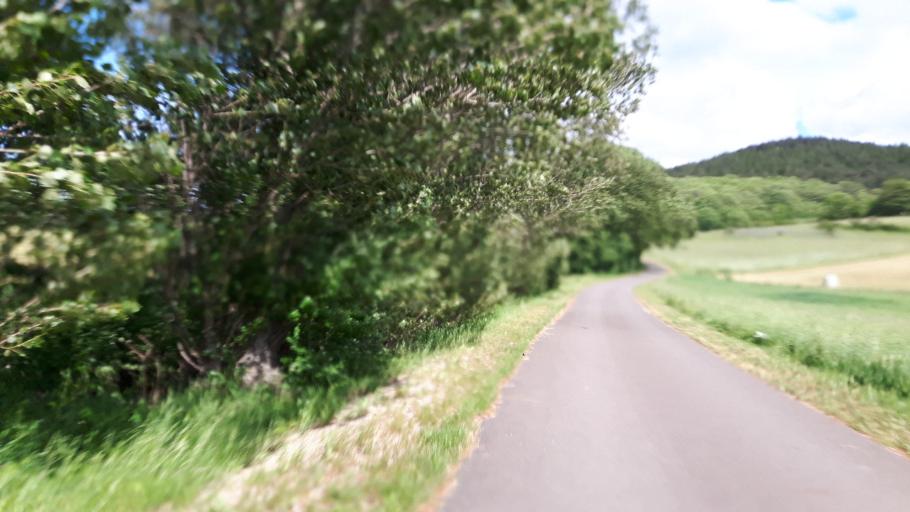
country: DE
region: Thuringia
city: Stadtilm
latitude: 50.7801
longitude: 11.1018
